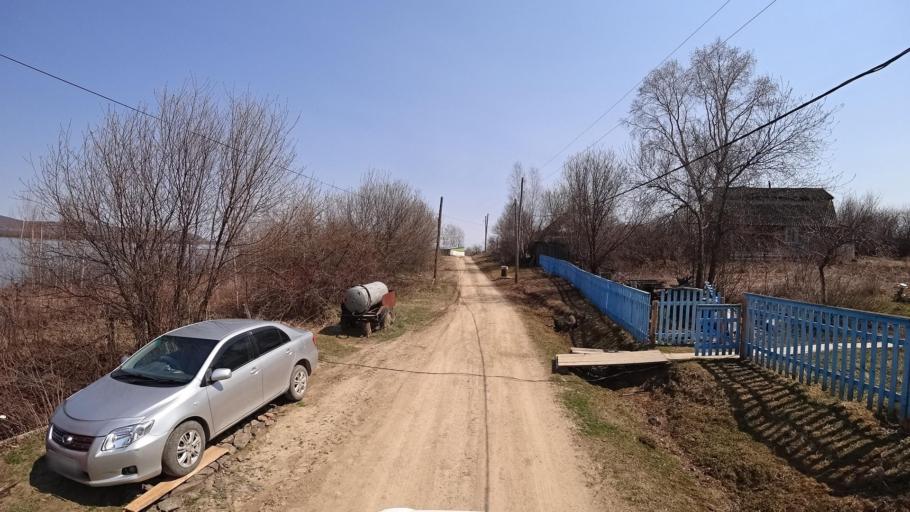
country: RU
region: Khabarovsk Krai
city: Selikhino
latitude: 50.6707
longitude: 137.3955
